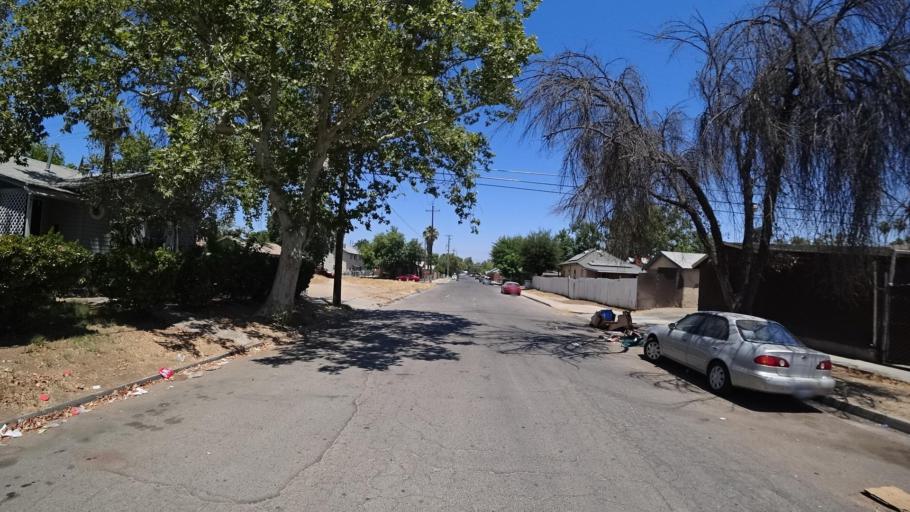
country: US
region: California
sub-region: Fresno County
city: Fresno
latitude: 36.7548
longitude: -119.7835
